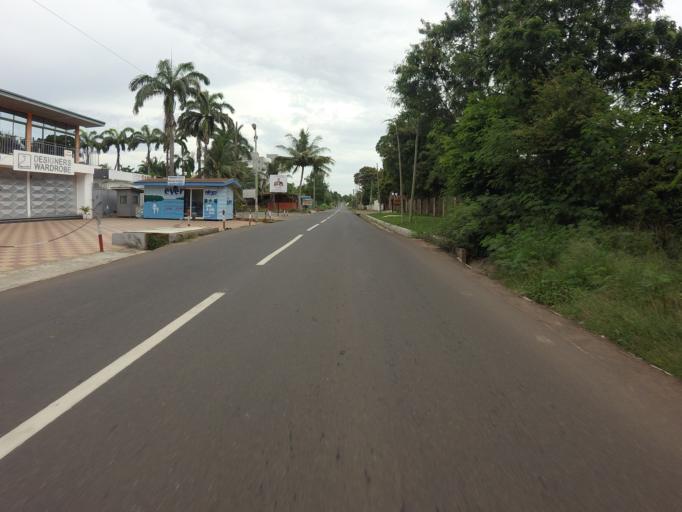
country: GH
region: Greater Accra
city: Dome
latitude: 5.6111
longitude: -0.2099
